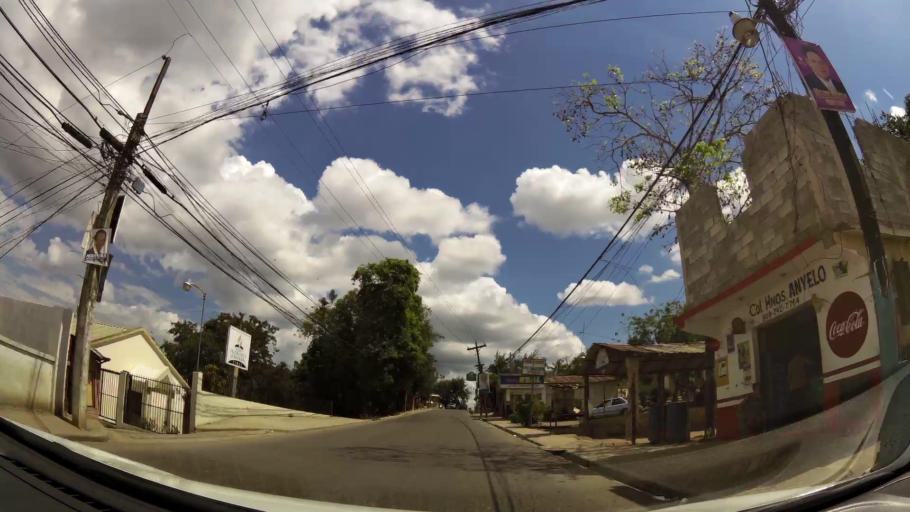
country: DO
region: Santiago
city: Santiago de los Caballeros
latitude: 19.4105
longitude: -70.6728
